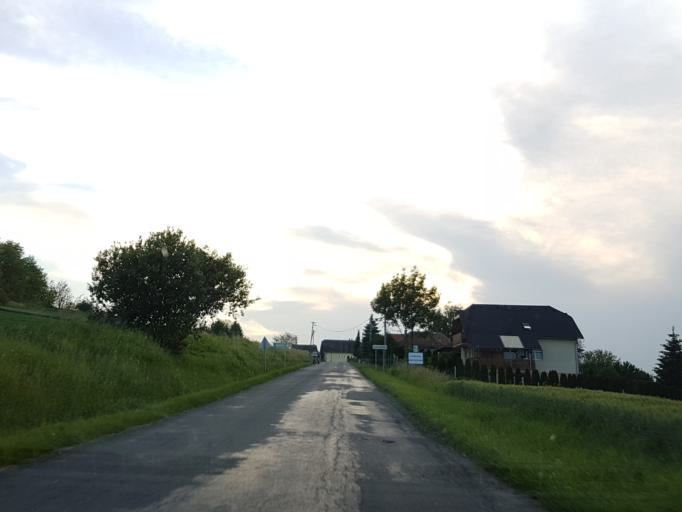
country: HU
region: Zala
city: Zalaegerszeg
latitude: 46.8679
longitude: 16.7478
